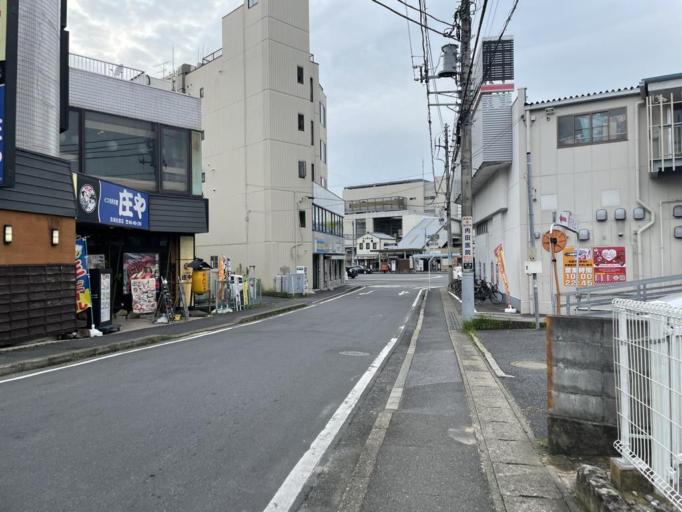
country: JP
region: Chiba
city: Sakura
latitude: 35.7242
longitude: 140.2302
